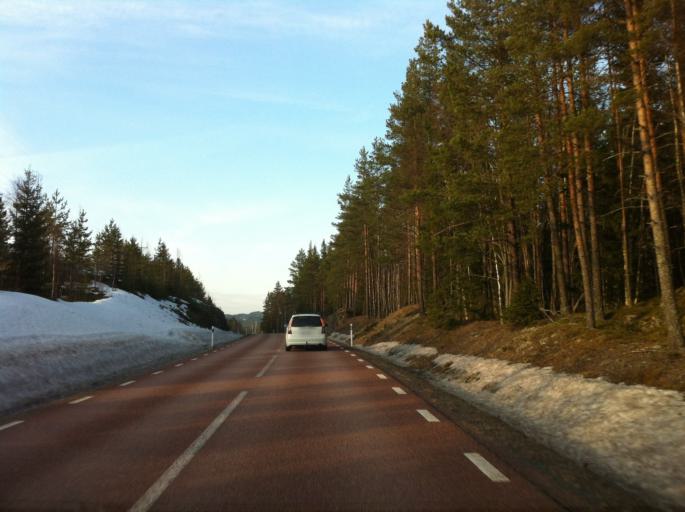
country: SE
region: Vaermland
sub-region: Filipstads Kommun
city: Lesjofors
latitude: 60.2283
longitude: 14.1792
